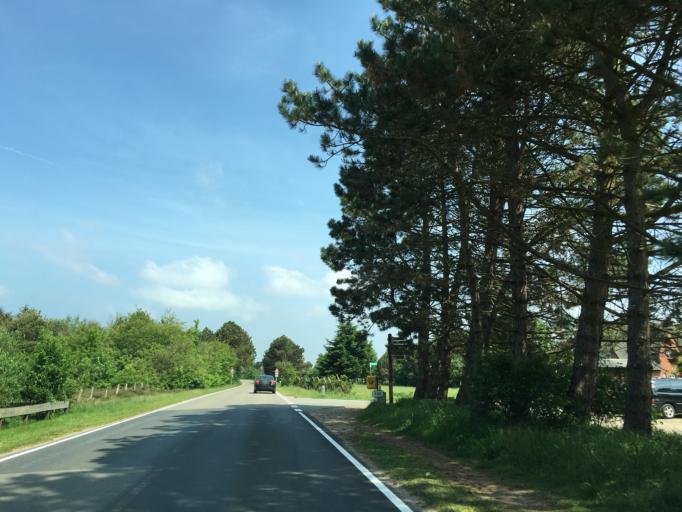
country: DE
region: Schleswig-Holstein
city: Nebel
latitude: 54.6510
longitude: 8.3457
